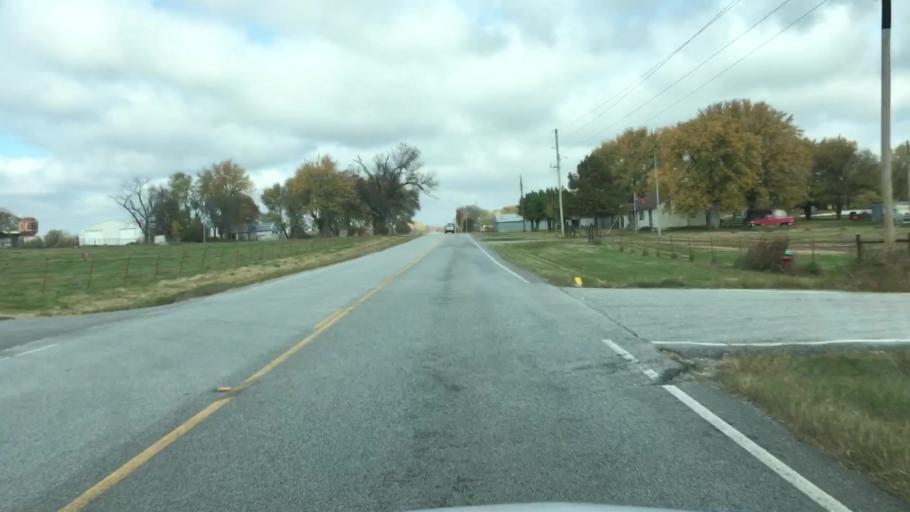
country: US
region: Arkansas
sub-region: Benton County
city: Centerton
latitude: 36.2724
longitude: -94.3502
